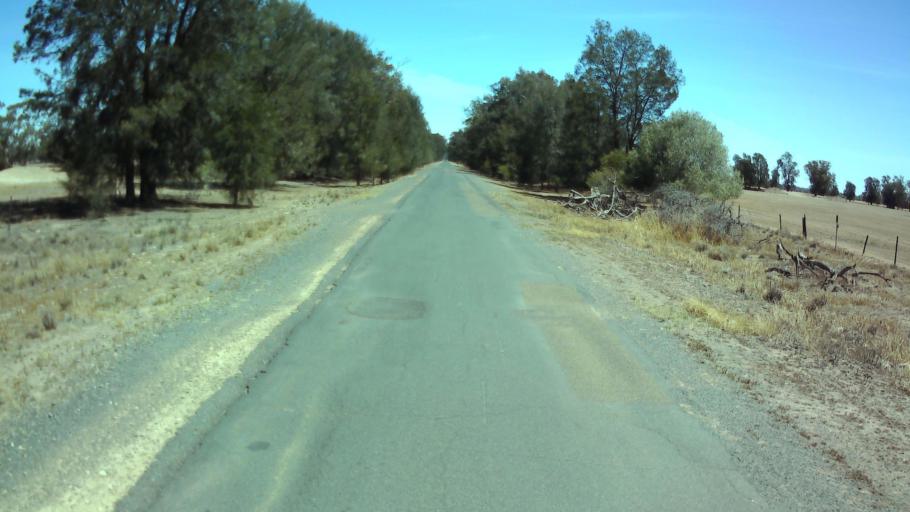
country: AU
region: New South Wales
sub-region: Weddin
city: Grenfell
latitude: -33.8761
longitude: 147.6911
